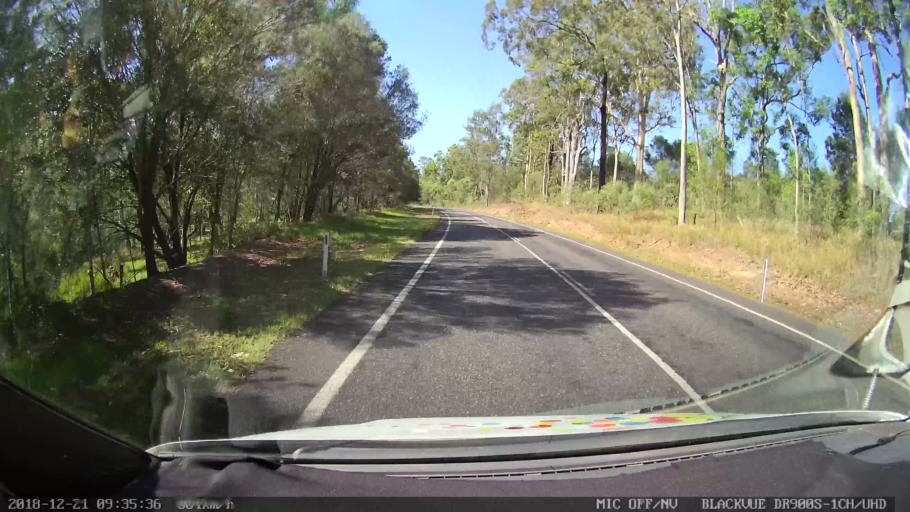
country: AU
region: New South Wales
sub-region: Clarence Valley
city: Grafton
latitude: -29.5128
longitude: 152.9806
